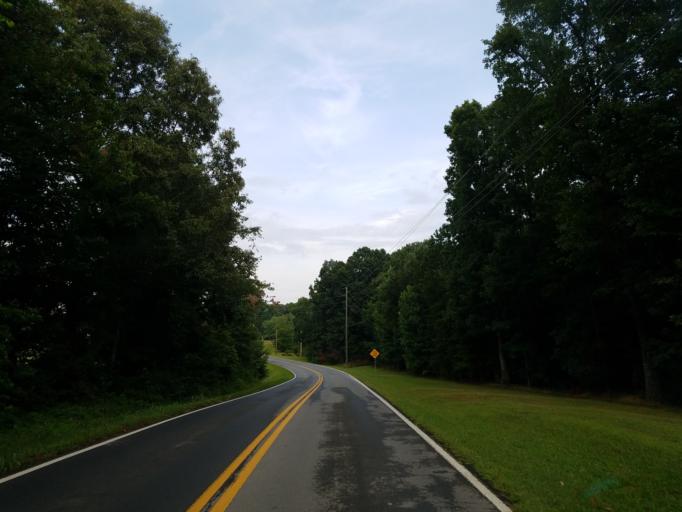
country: US
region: Georgia
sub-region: Pickens County
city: Jasper
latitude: 34.4571
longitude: -84.5377
